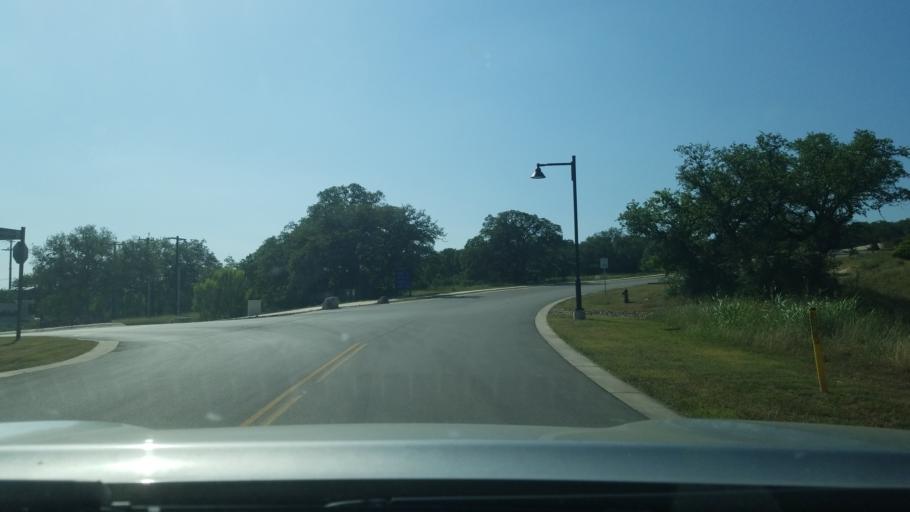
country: US
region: Texas
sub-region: Comal County
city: Bulverde
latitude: 29.7593
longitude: -98.4211
